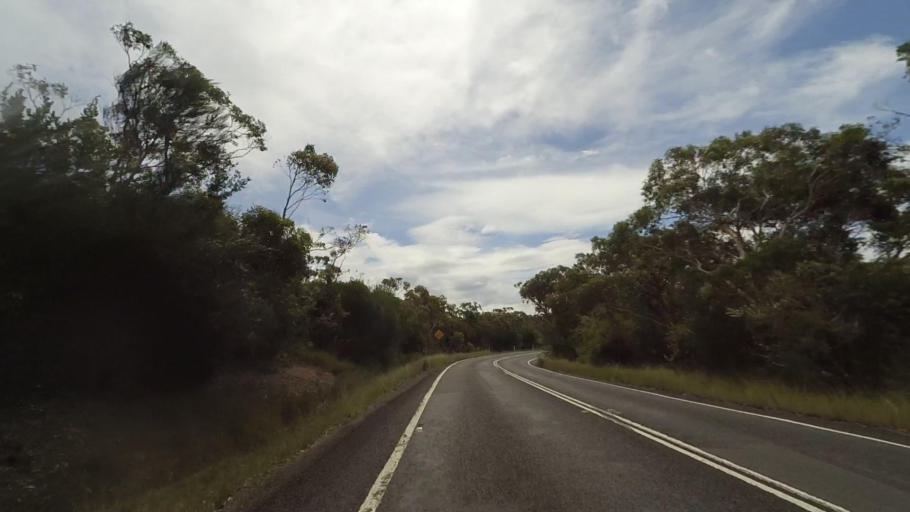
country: AU
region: New South Wales
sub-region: Sutherland Shire
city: Grays Point
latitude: -34.0848
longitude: 151.0644
